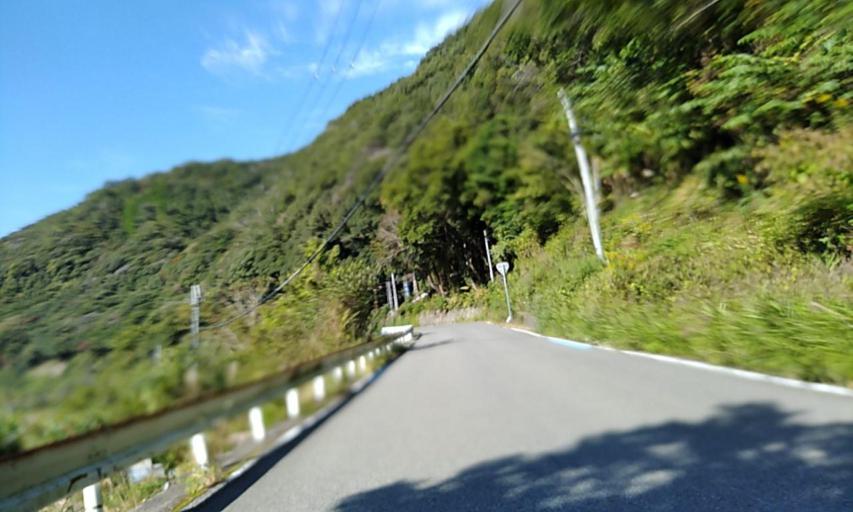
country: JP
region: Wakayama
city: Kainan
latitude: 34.0564
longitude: 135.3347
